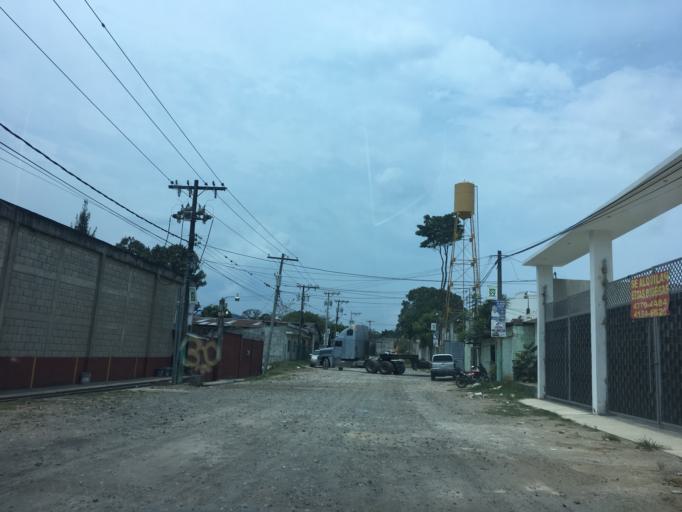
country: GT
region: Guatemala
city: Petapa
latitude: 14.5072
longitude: -90.5569
